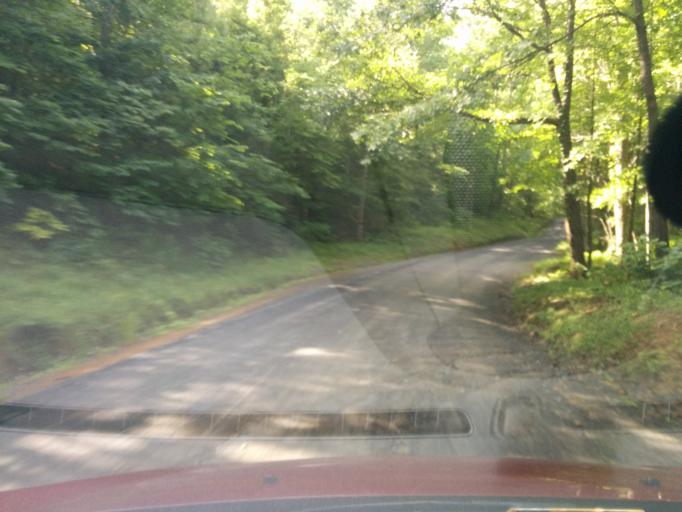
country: US
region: Virginia
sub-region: City of Lexington
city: Lexington
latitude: 37.7838
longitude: -79.5016
